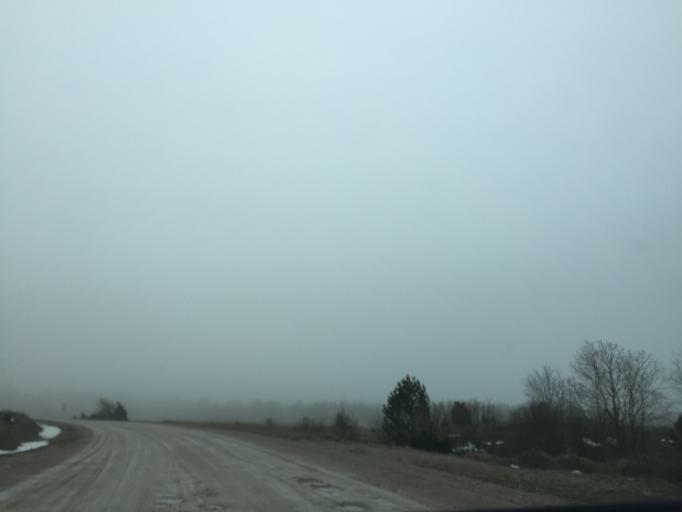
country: EE
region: Saare
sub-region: Kuressaare linn
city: Kuressaare
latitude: 58.4672
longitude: 22.0016
